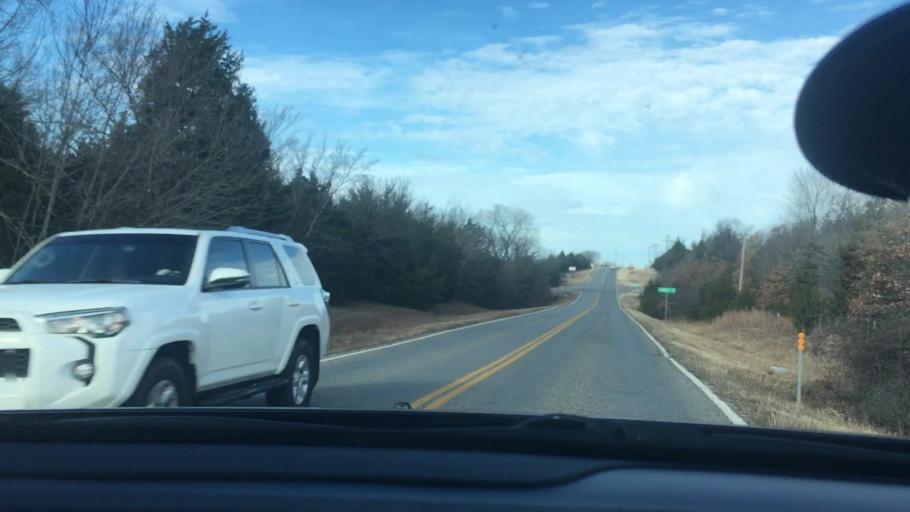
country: US
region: Oklahoma
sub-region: Seminole County
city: Konawa
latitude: 34.9682
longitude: -96.7736
